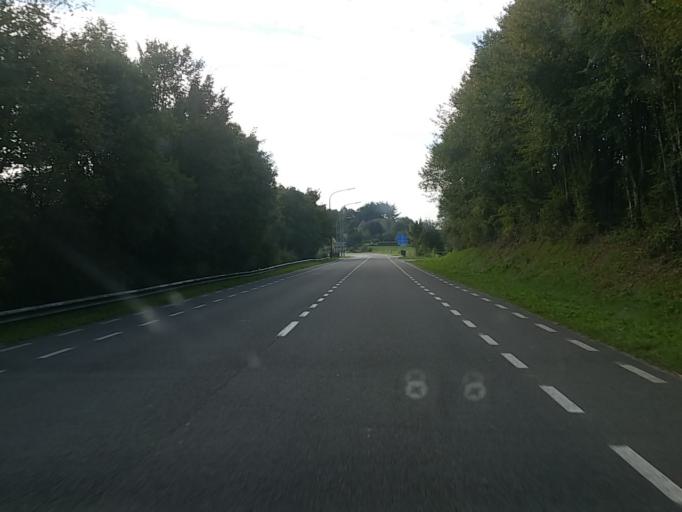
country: BE
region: Wallonia
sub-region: Province du Luxembourg
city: Florenville
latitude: 49.7043
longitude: 5.2587
